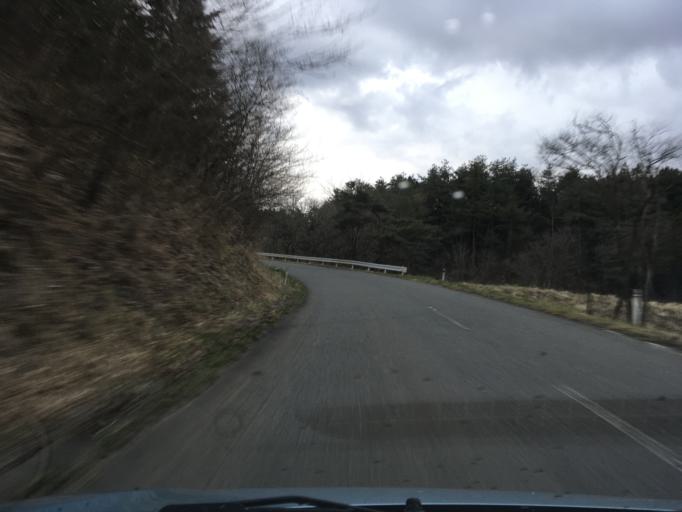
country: JP
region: Iwate
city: Ichinoseki
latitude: 38.7812
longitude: 141.2430
